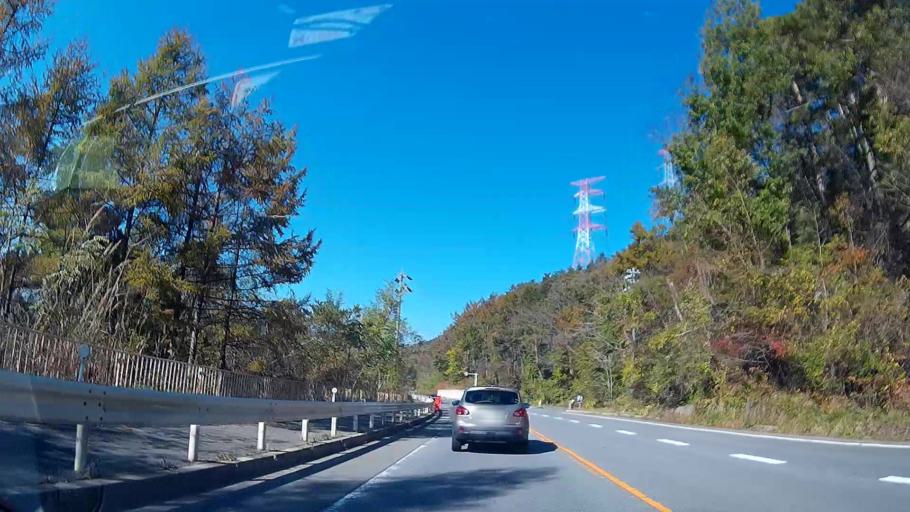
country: JP
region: Nagano
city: Okaya
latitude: 36.0876
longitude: 138.0264
